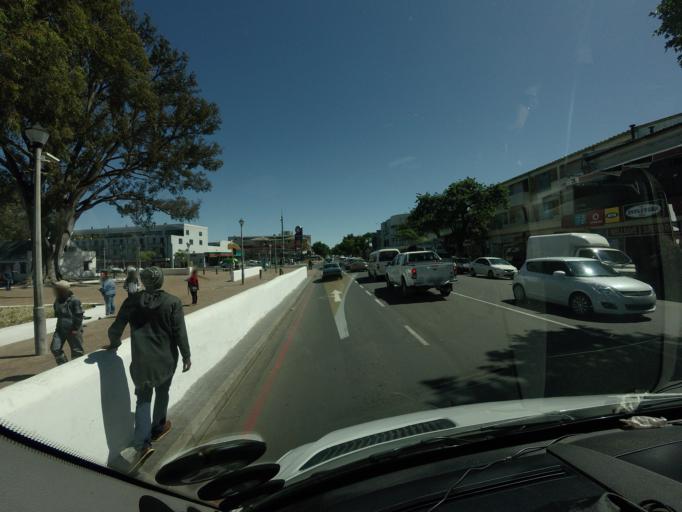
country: ZA
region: Western Cape
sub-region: Cape Winelands District Municipality
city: Stellenbosch
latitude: -33.9325
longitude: 18.8588
